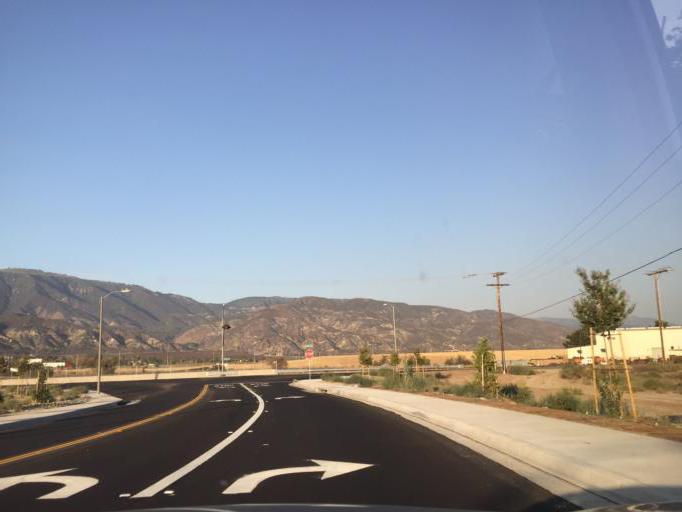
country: US
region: California
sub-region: San Bernardino County
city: Muscoy
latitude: 34.1863
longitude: -117.3643
